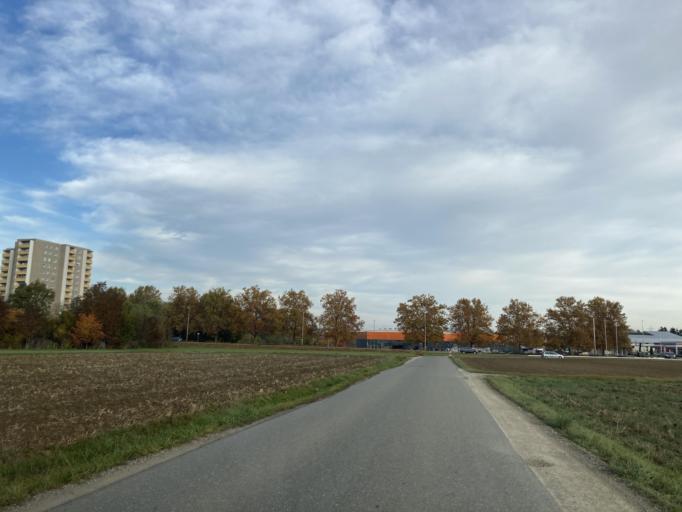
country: DE
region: Baden-Wuerttemberg
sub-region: Tuebingen Region
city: Ofterdingen
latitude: 48.4026
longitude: 9.0388
